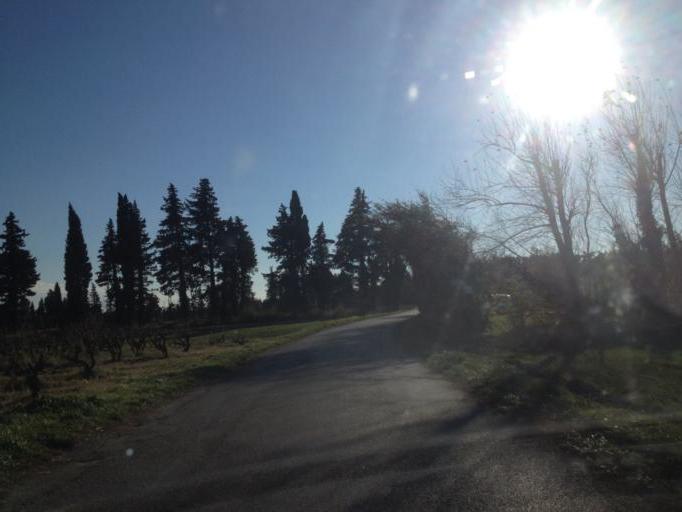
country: FR
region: Provence-Alpes-Cote d'Azur
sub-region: Departement du Vaucluse
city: Courthezon
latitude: 44.0860
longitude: 4.9089
